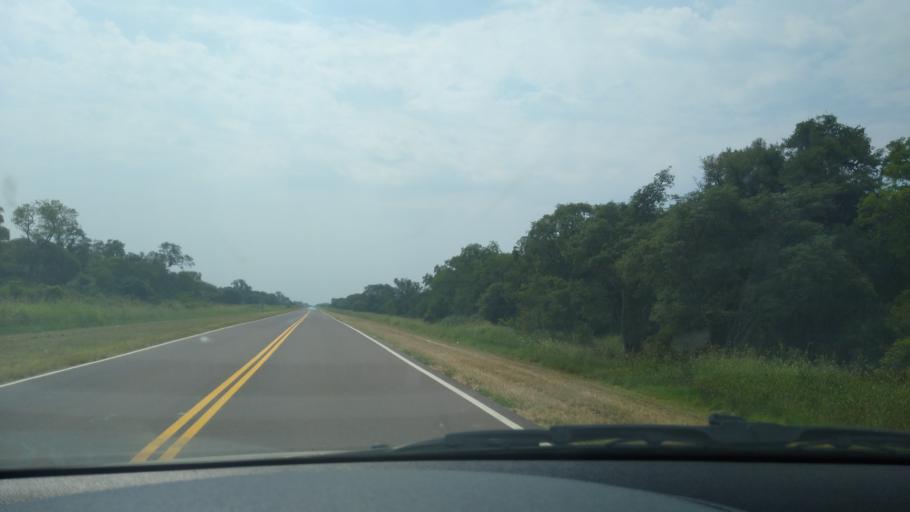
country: AR
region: Chaco
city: Margarita Belen
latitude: -27.0453
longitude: -58.9627
